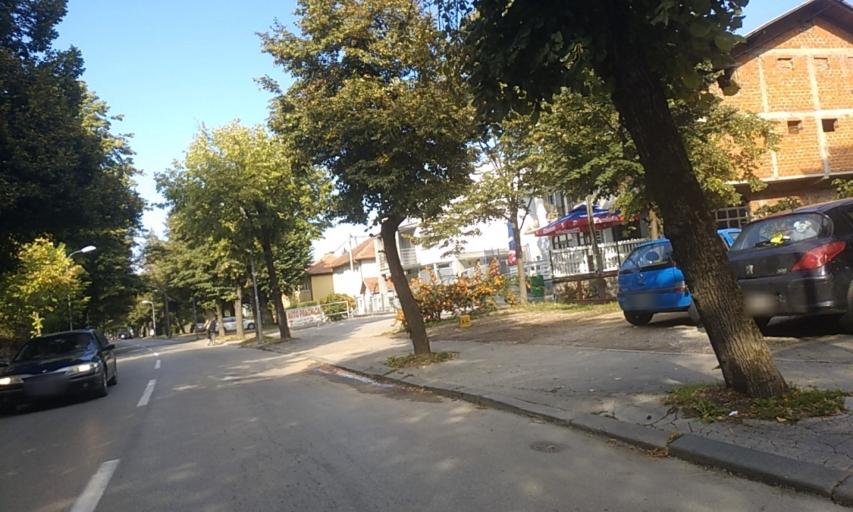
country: BA
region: Republika Srpska
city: Hiseti
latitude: 44.7576
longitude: 17.1783
